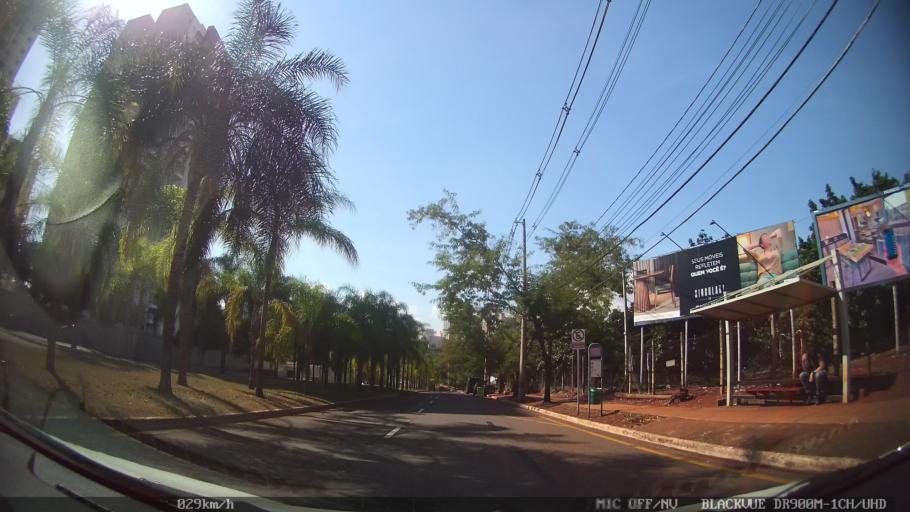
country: BR
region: Sao Paulo
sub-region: Ribeirao Preto
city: Ribeirao Preto
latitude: -21.2248
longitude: -47.8326
